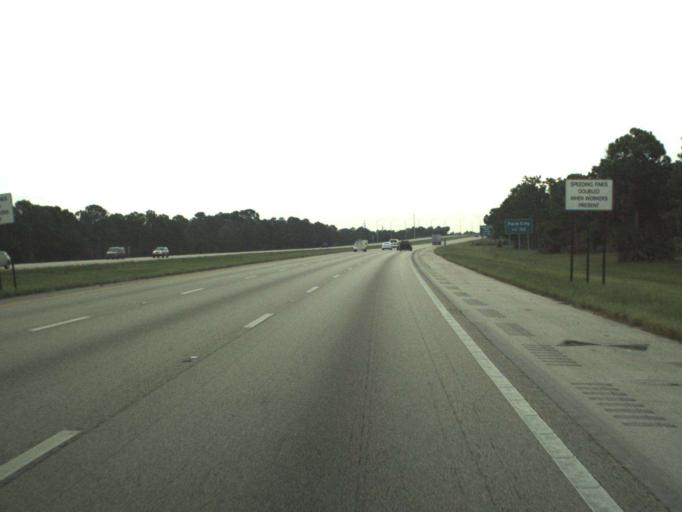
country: US
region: Florida
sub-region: Martin County
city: Palm City
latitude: 27.1268
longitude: -80.2898
